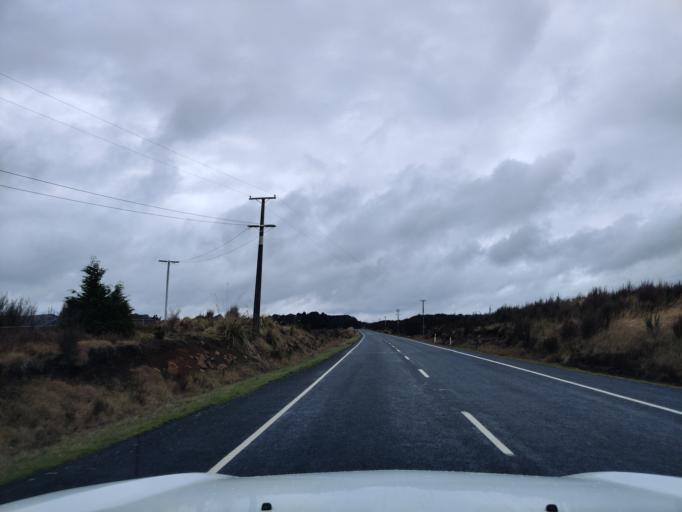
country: NZ
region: Manawatu-Wanganui
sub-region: Ruapehu District
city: Waiouru
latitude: -39.3406
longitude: 175.3783
